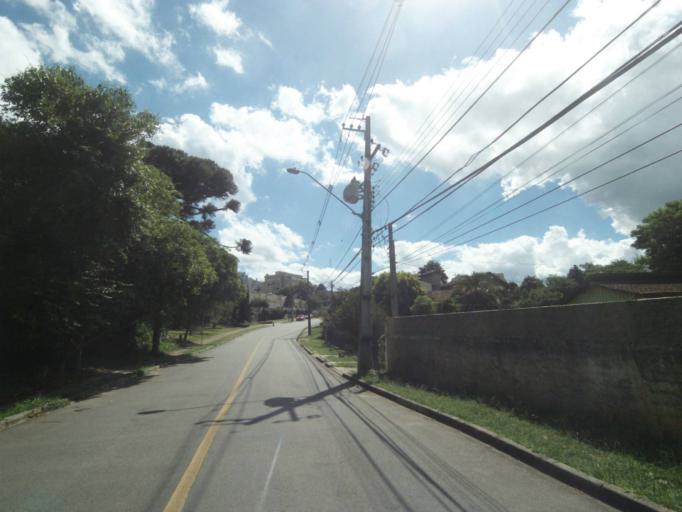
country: BR
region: Parana
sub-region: Curitiba
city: Curitiba
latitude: -25.4364
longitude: -49.3392
